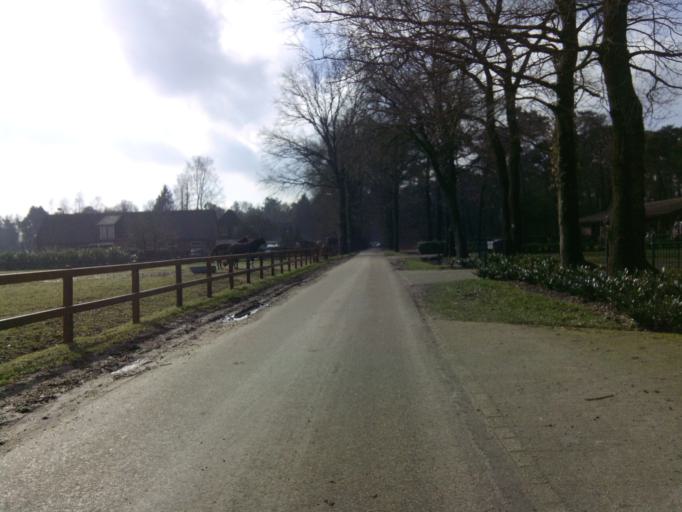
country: NL
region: Utrecht
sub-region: Gemeente Utrechtse Heuvelrug
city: Leersum
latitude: 52.0456
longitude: 5.4504
